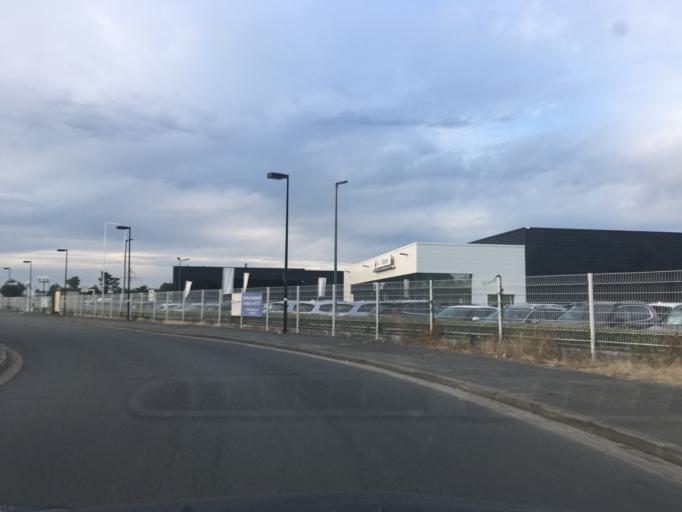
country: FR
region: Aquitaine
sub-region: Departement de la Gironde
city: Le Haillan
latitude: 44.8471
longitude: -0.6675
